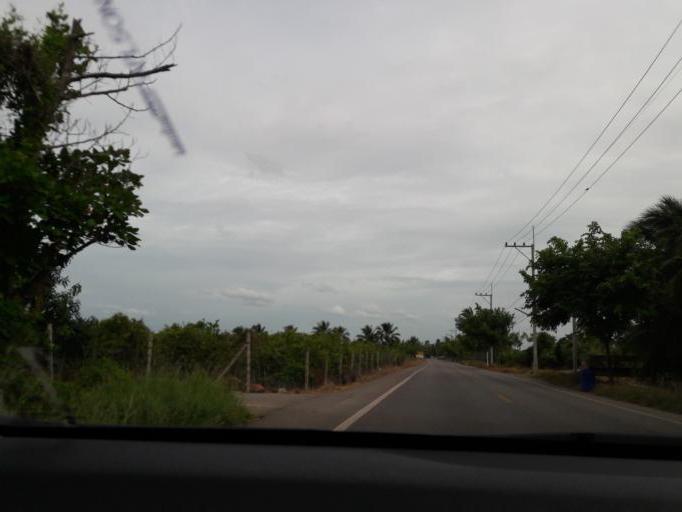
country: TH
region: Samut Sakhon
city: Ban Phaeo
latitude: 13.5640
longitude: 100.0441
